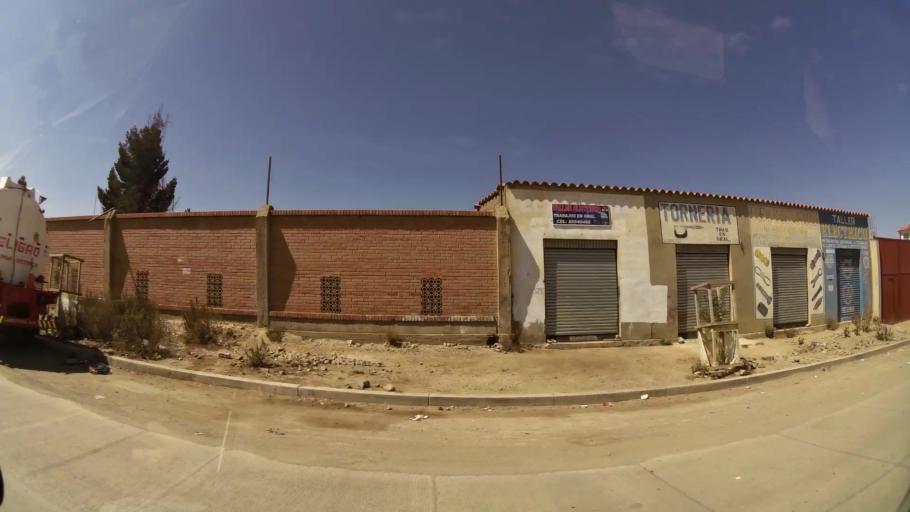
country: BO
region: La Paz
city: La Paz
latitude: -16.5460
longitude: -68.1799
